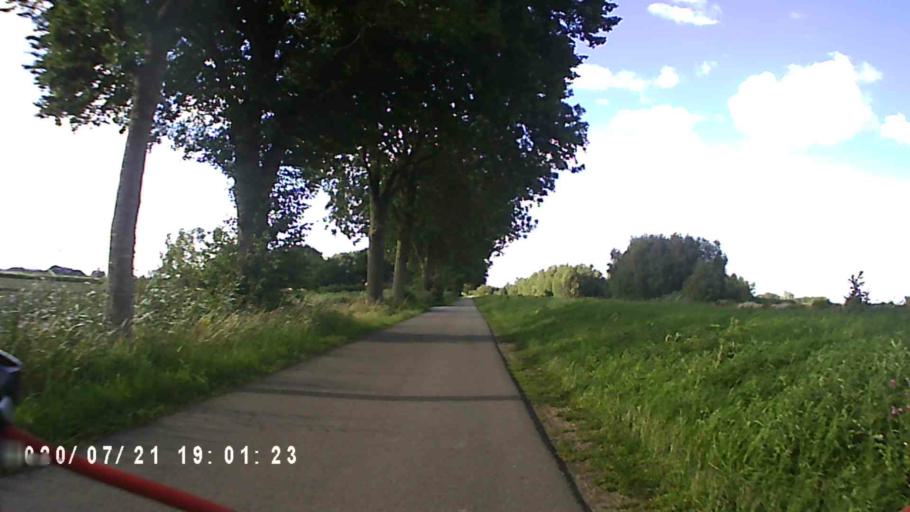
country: NL
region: Groningen
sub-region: Gemeente Slochteren
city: Slochteren
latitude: 53.2268
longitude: 6.7394
